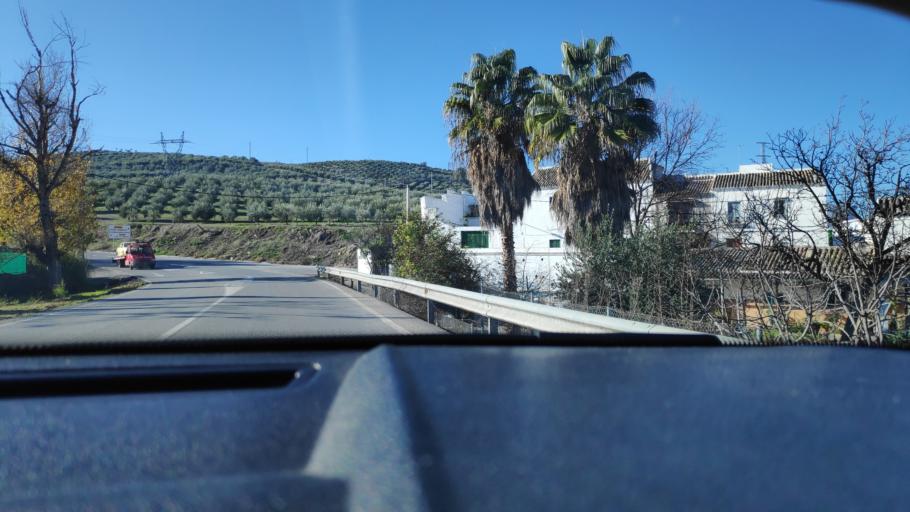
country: ES
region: Andalusia
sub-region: Province of Cordoba
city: Baena
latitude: 37.6108
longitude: -4.3227
